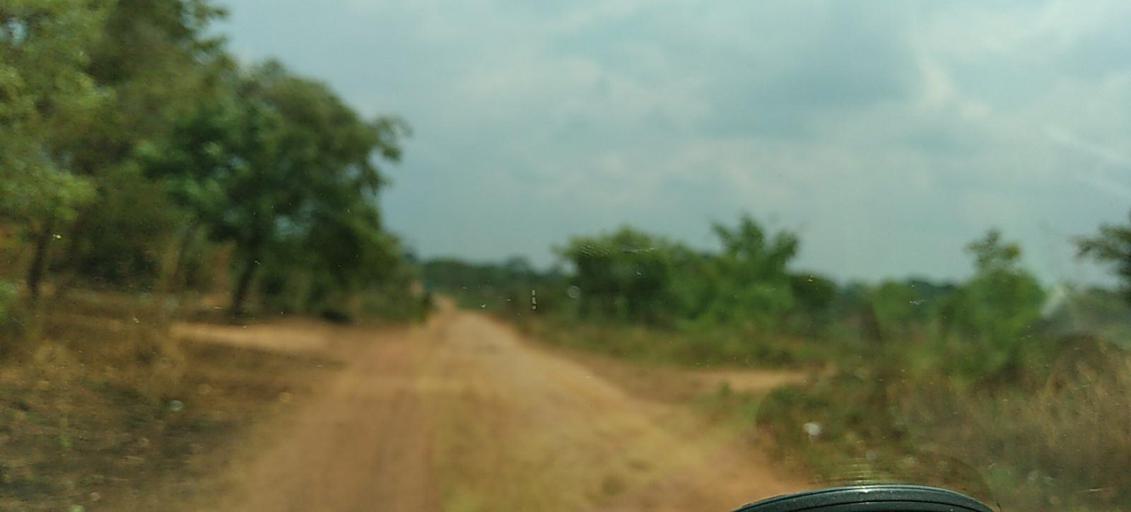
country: ZM
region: North-Western
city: Kansanshi
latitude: -11.9925
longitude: 26.2826
